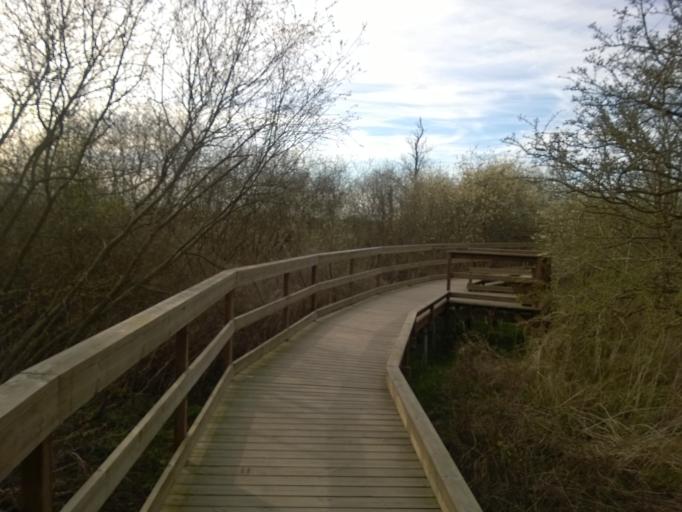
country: SE
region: Skane
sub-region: Kristianstads Kommun
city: Kristianstad
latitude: 56.0328
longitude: 14.1469
